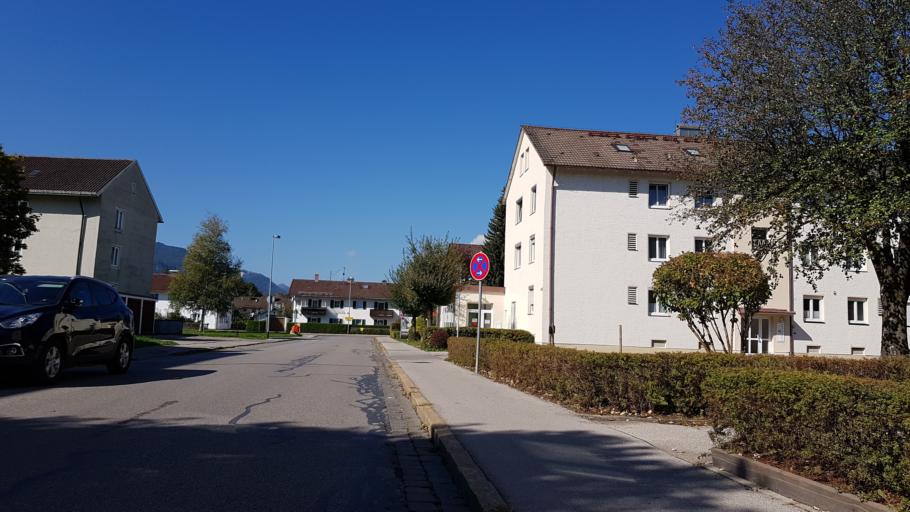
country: DE
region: Bavaria
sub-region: Swabia
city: Fuessen
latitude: 47.5733
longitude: 10.6792
